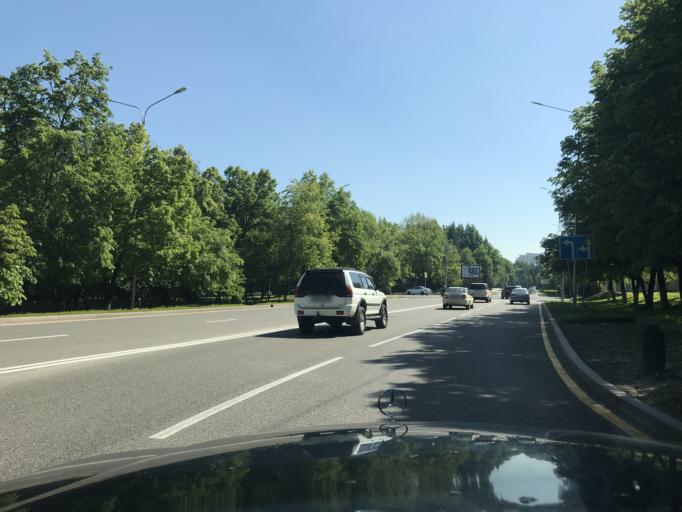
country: KZ
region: Almaty Qalasy
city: Almaty
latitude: 43.2352
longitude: 76.9410
